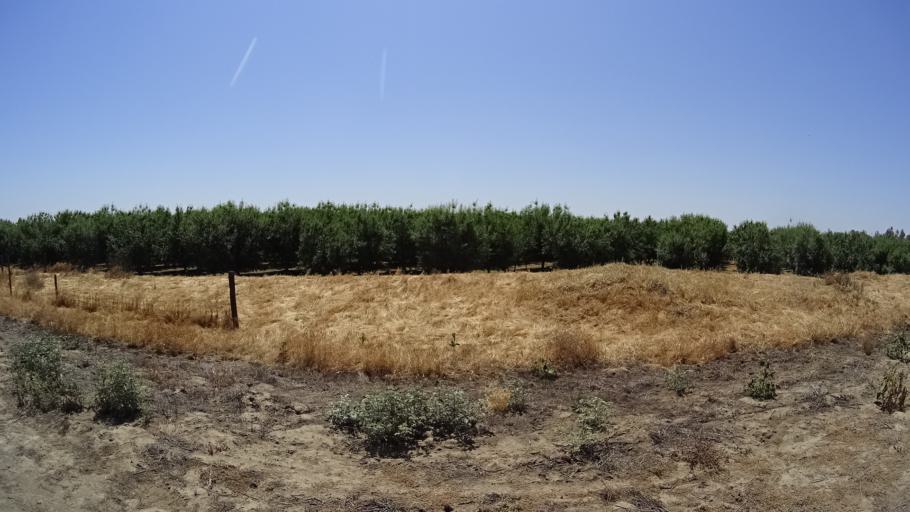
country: US
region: California
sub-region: Kings County
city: Lemoore
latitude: 36.3641
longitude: -119.8068
